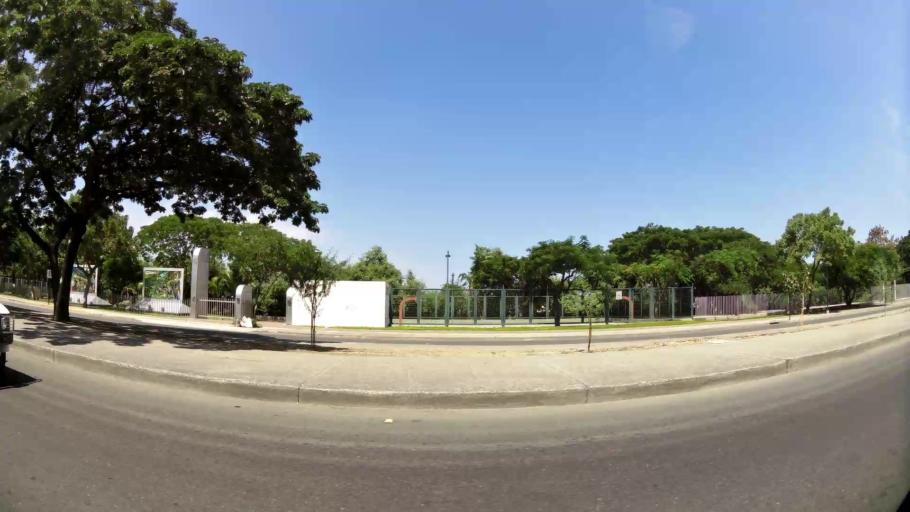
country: EC
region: Guayas
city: Guayaquil
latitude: -2.1887
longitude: -79.9175
